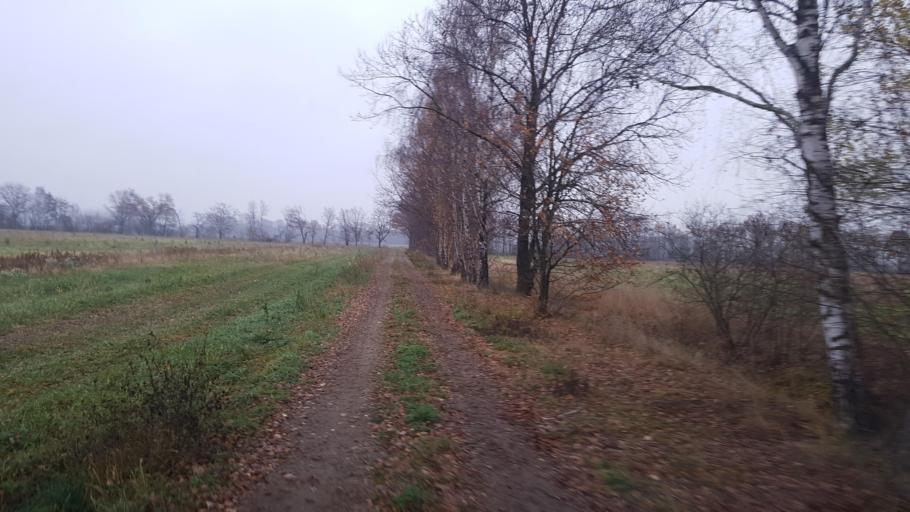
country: DE
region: Brandenburg
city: Lindenau
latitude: 51.4089
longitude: 13.7113
